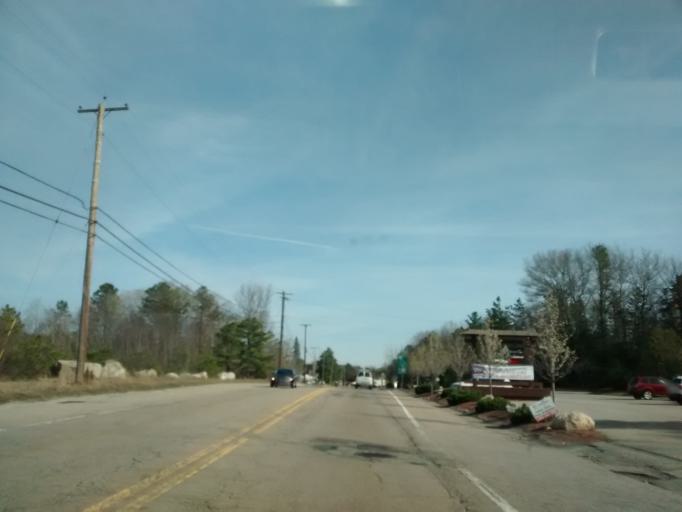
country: US
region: Massachusetts
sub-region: Worcester County
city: Millville
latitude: 42.0278
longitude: -71.6063
